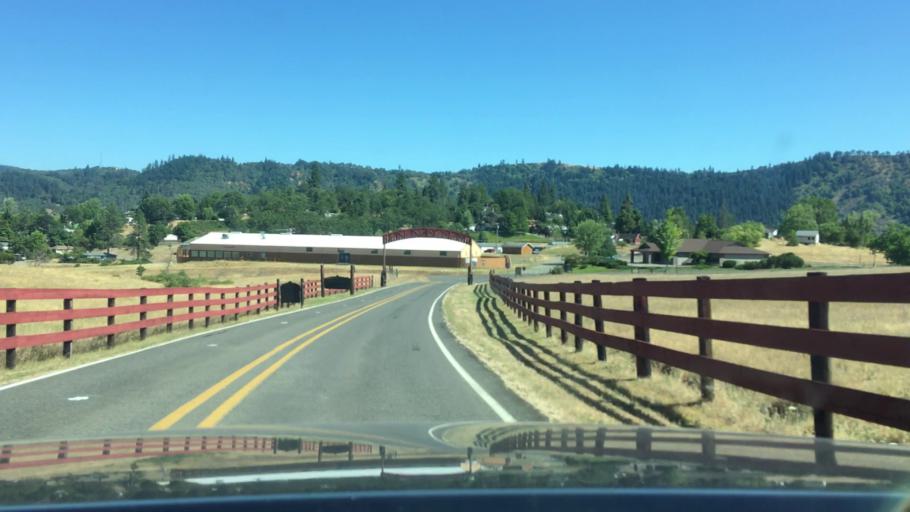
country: US
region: Oregon
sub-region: Douglas County
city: Winston
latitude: 43.1297
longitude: -123.4134
